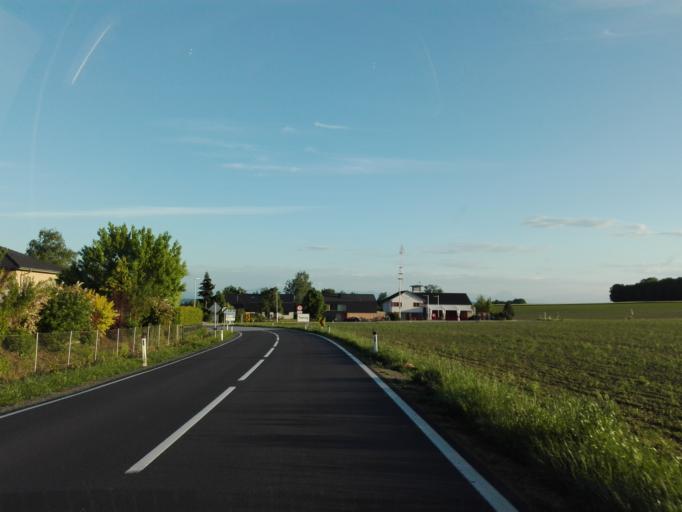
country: AT
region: Upper Austria
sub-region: Politischer Bezirk Linz-Land
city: Horsching
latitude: 48.2583
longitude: 14.1575
